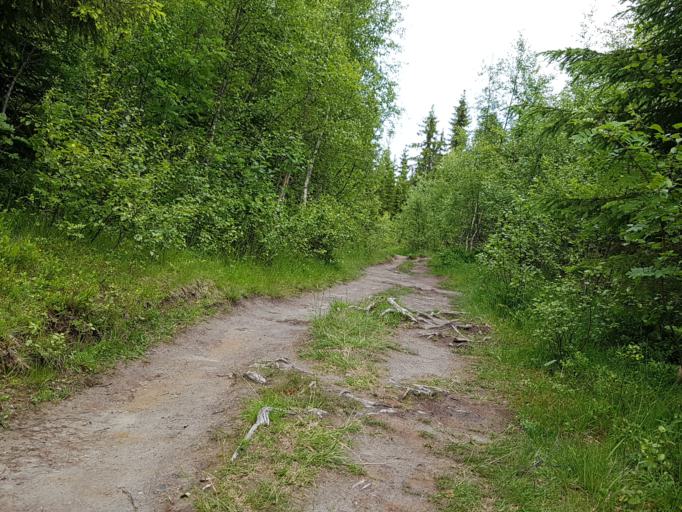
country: NO
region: Sor-Trondelag
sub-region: Melhus
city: Melhus
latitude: 63.4013
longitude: 10.2790
